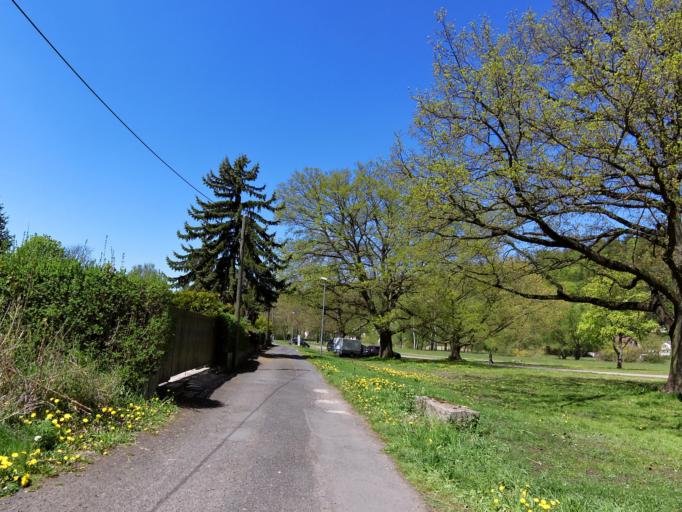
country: DE
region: Thuringia
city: Bad Salzungen
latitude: 50.8174
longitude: 10.2378
